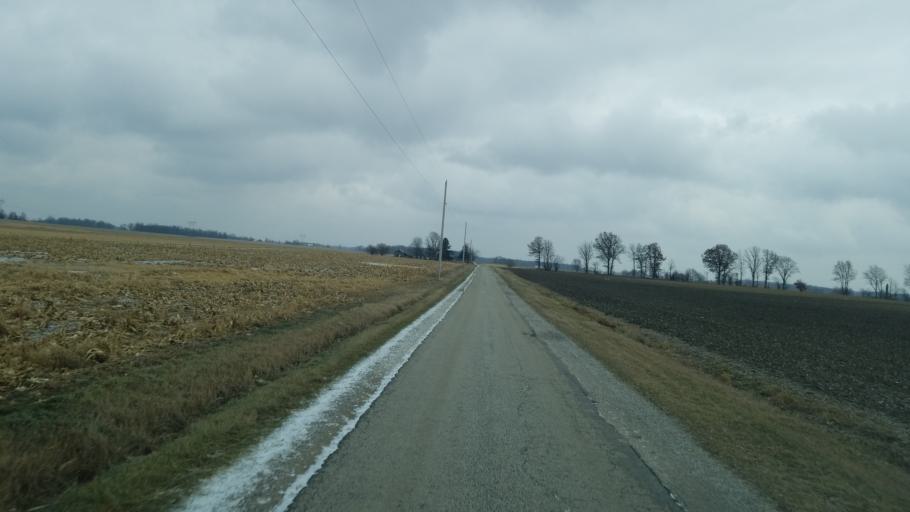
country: US
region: Ohio
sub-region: Crawford County
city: Bucyrus
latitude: 40.7466
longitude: -82.9822
